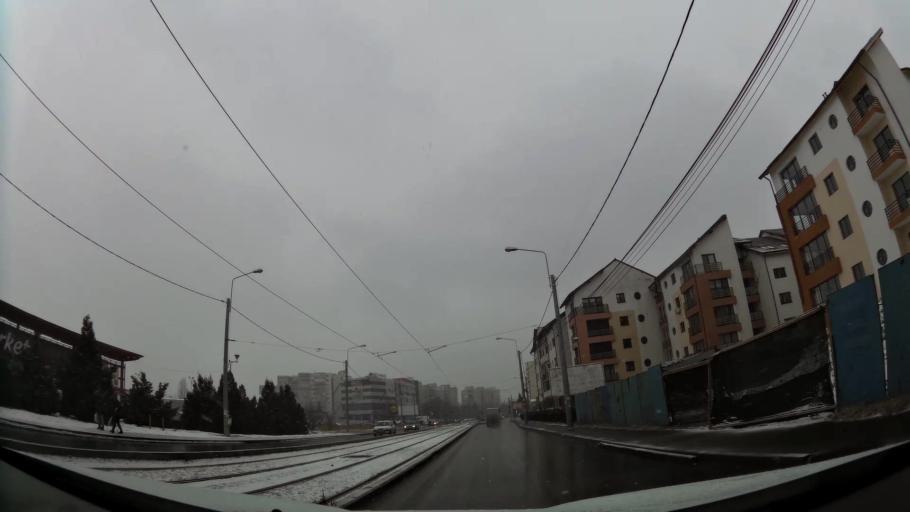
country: RO
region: Prahova
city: Ploiesti
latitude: 44.9274
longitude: 25.9935
